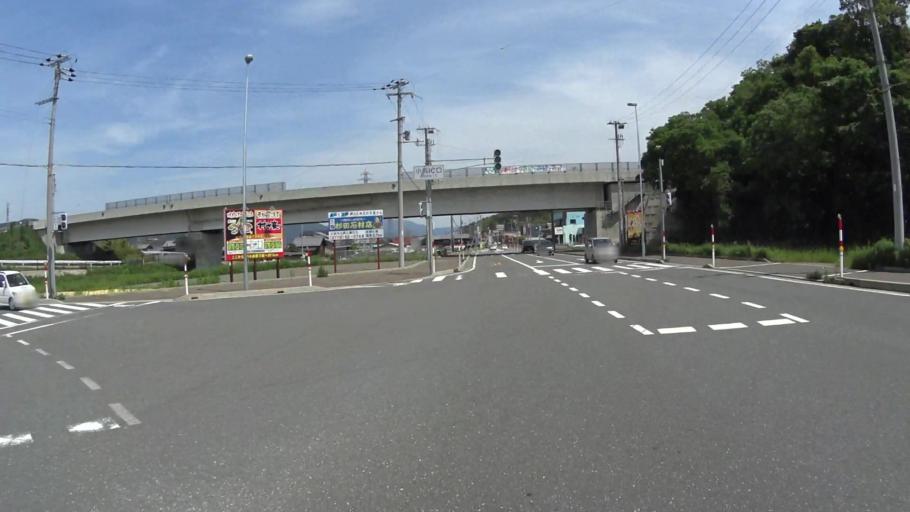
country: JP
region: Fukui
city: Obama
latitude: 35.4870
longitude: 135.7631
